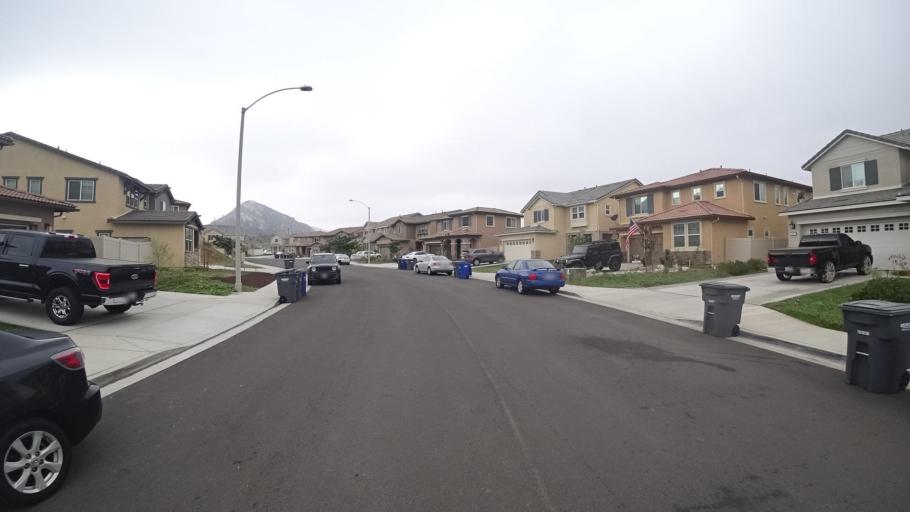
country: US
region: California
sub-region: San Diego County
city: Rainbow
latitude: 33.3537
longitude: -117.1513
